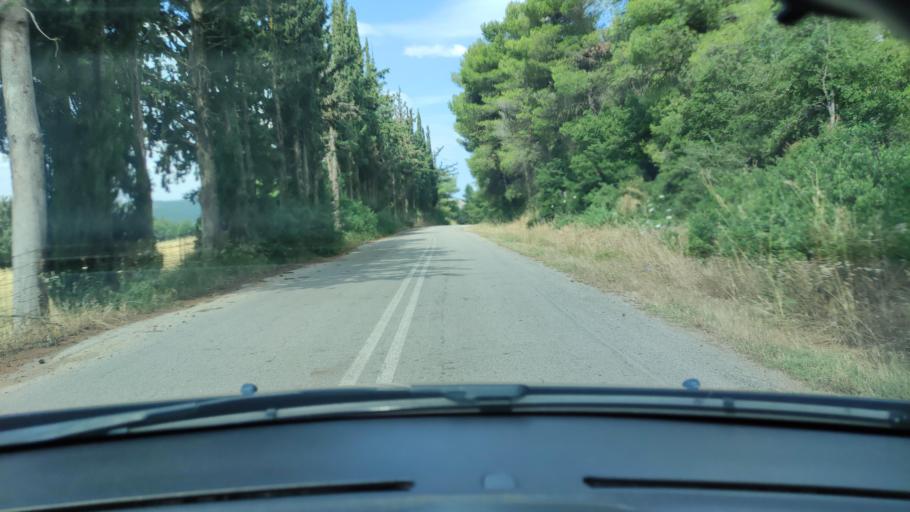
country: GR
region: Central Greece
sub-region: Nomos Evvoias
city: Afration
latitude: 38.5192
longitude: 23.7568
